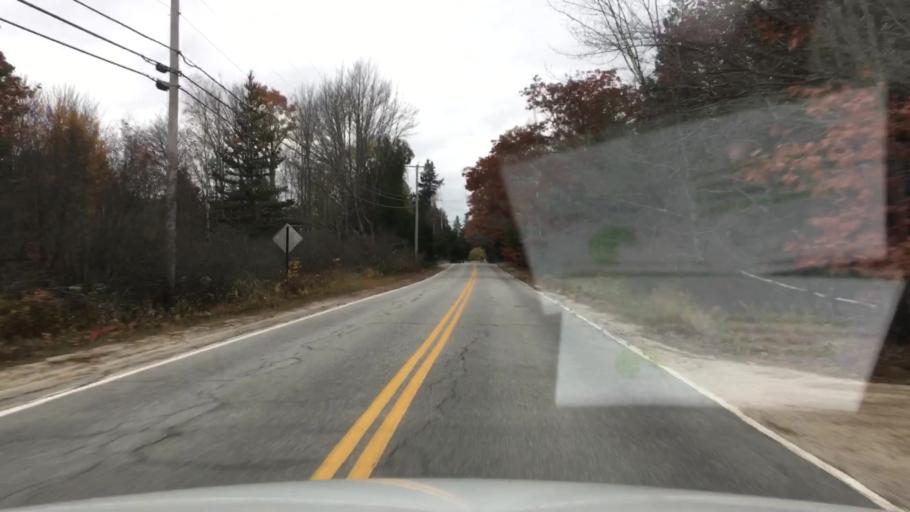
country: US
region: Maine
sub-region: Hancock County
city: Sedgwick
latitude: 44.3688
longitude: -68.5553
